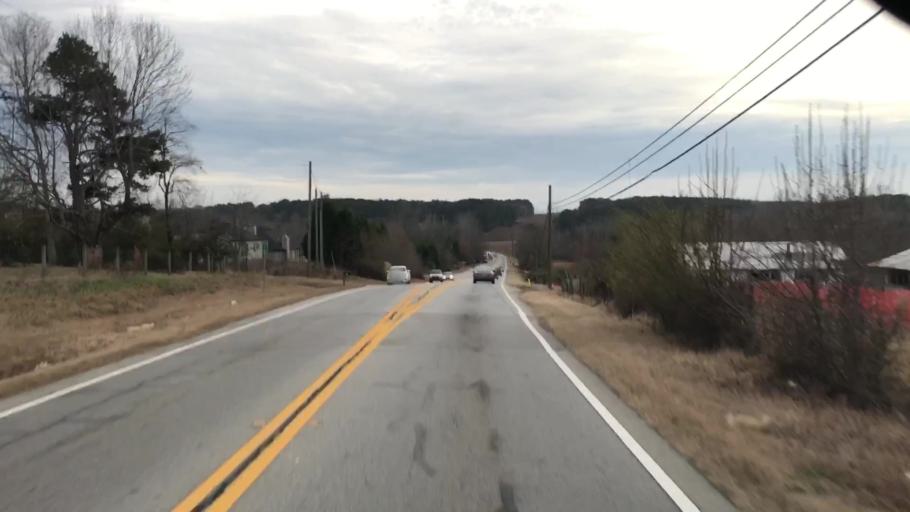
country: US
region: Georgia
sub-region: Barrow County
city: Winder
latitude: 34.0118
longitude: -83.7573
